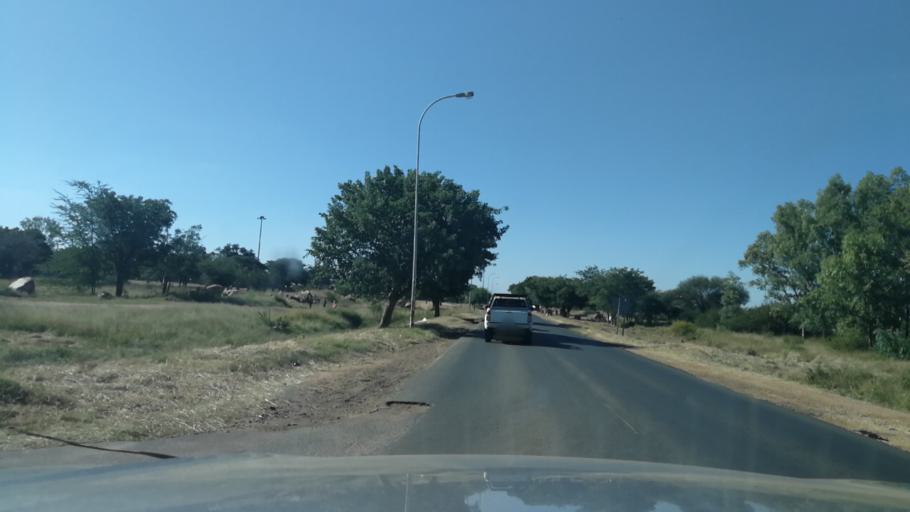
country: BW
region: South East
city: Gaborone
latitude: -24.6915
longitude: 25.8992
